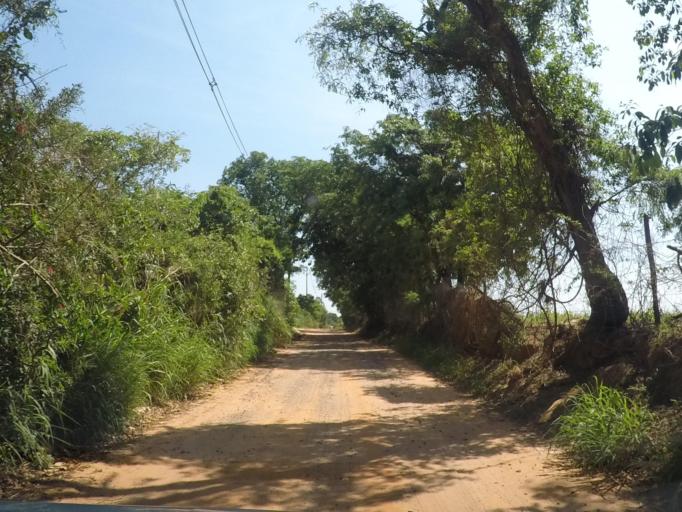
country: BR
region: Sao Paulo
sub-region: Sumare
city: Sumare
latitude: -22.8788
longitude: -47.2883
